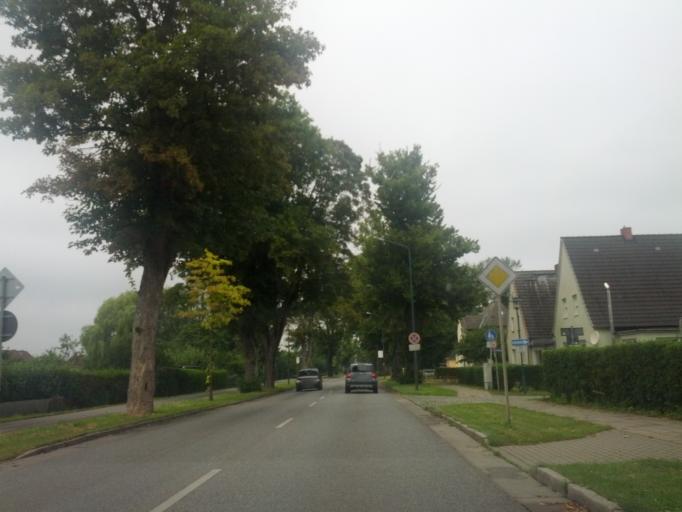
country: DE
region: Mecklenburg-Vorpommern
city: Hornstorf
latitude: 53.8927
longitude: 11.5036
